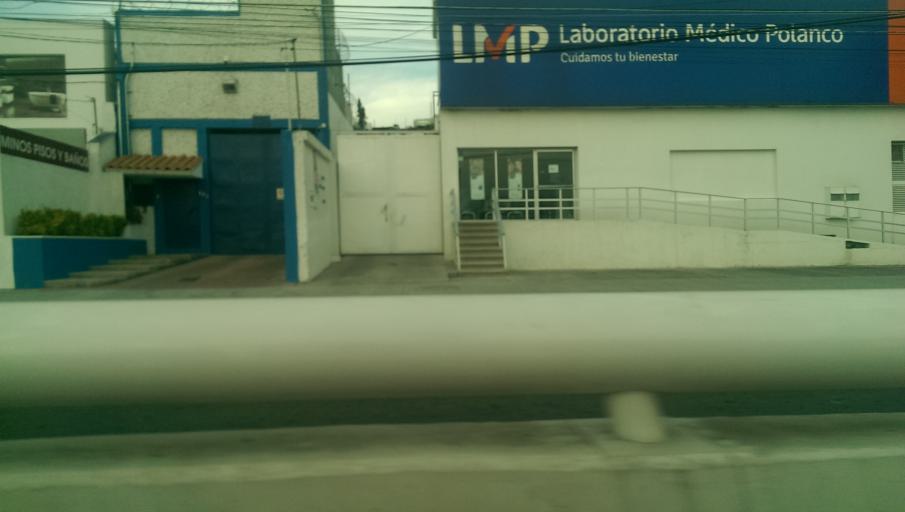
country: MX
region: Queretaro
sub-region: Queretaro
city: Santiago de Queretaro
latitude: 20.5934
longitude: -100.3688
